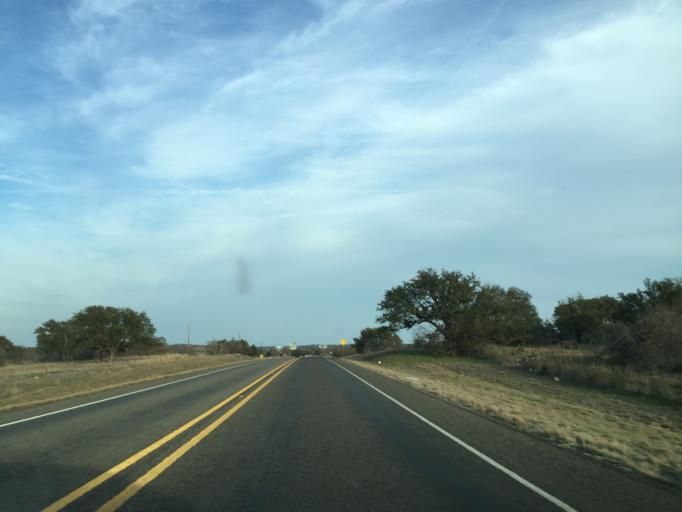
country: US
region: Texas
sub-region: Llano County
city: Llano
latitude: 30.7617
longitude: -98.6398
